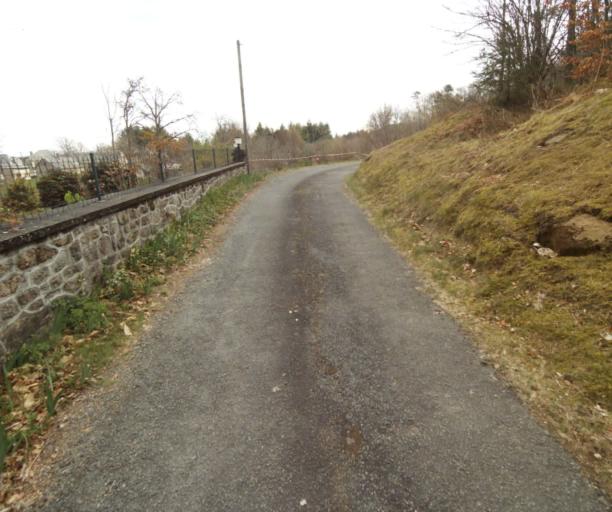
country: FR
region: Limousin
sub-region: Departement de la Correze
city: Correze
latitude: 45.3290
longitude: 1.9512
